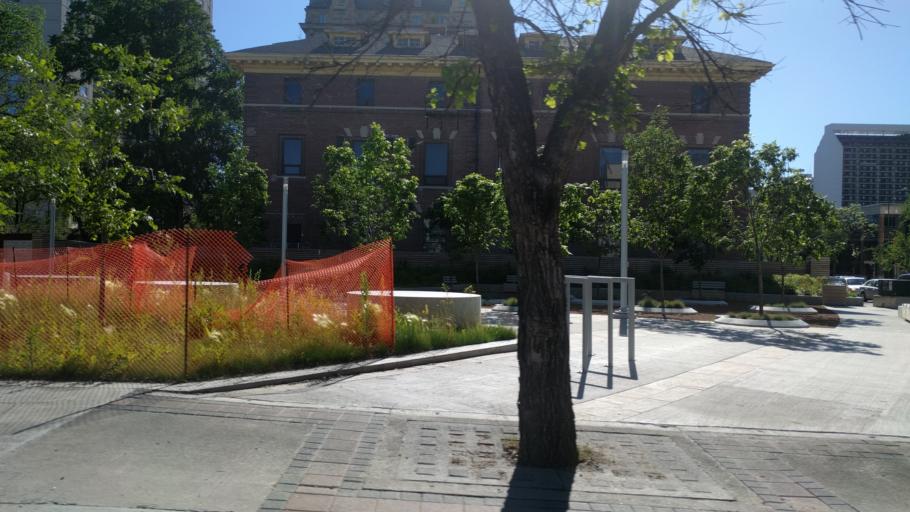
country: CA
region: Manitoba
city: Winnipeg
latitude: 49.8887
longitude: -97.1351
